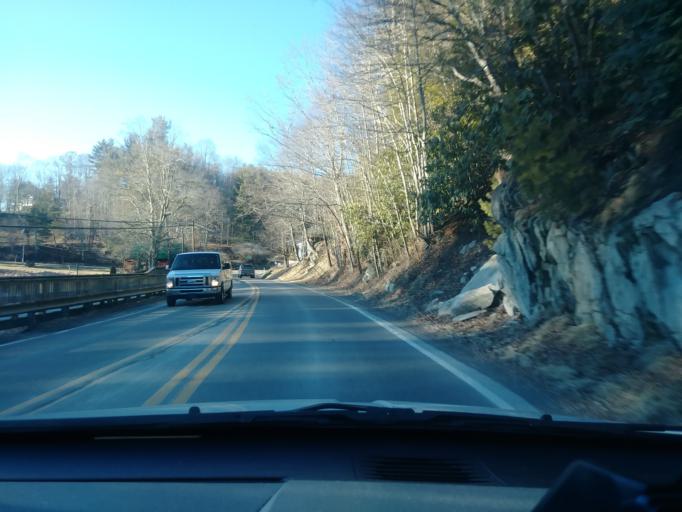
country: US
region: North Carolina
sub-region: Avery County
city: Banner Elk
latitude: 36.1573
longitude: -81.8696
